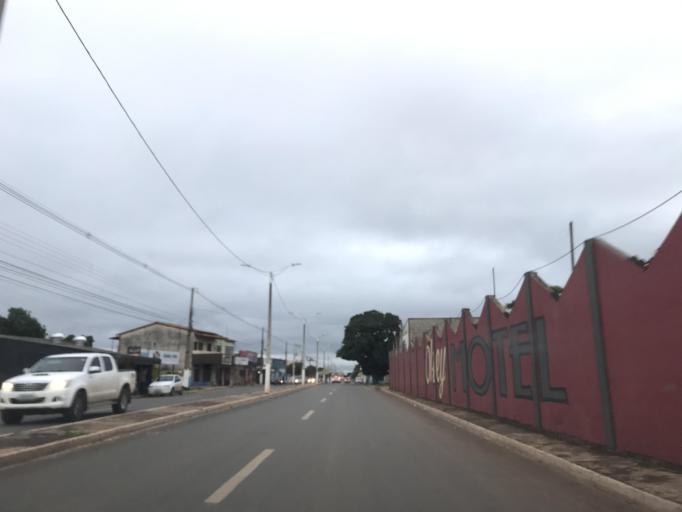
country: BR
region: Goias
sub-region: Luziania
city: Luziania
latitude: -16.2090
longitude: -47.9273
